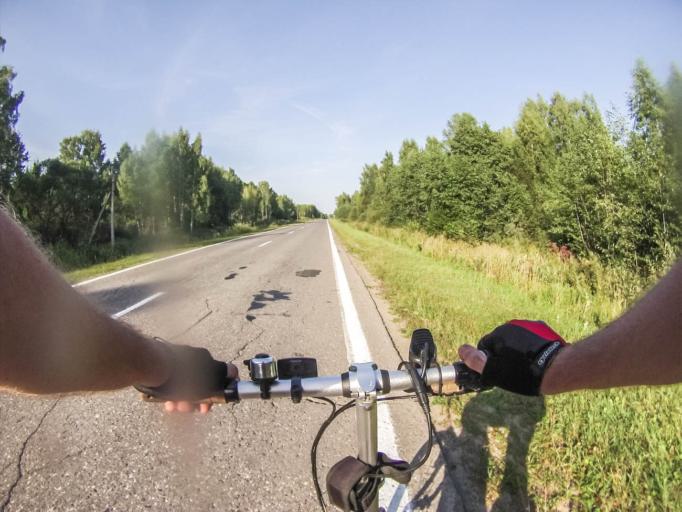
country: RU
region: Jaroslavl
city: Myshkin
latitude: 57.6881
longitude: 38.3328
